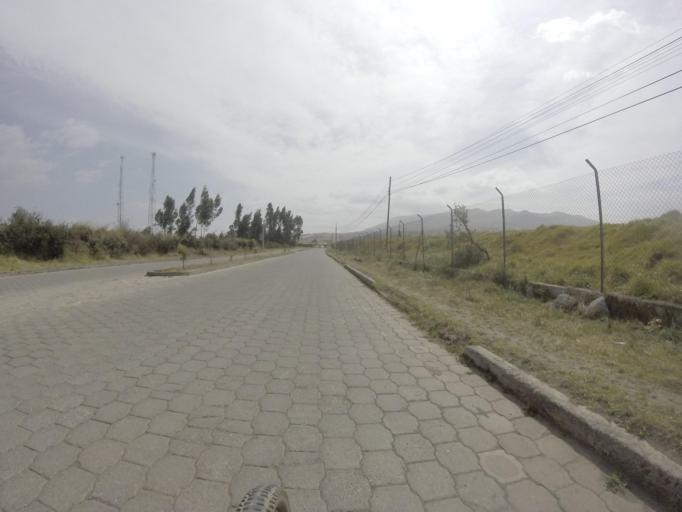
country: EC
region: Pichincha
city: Cayambe
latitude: 0.1461
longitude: -78.0711
